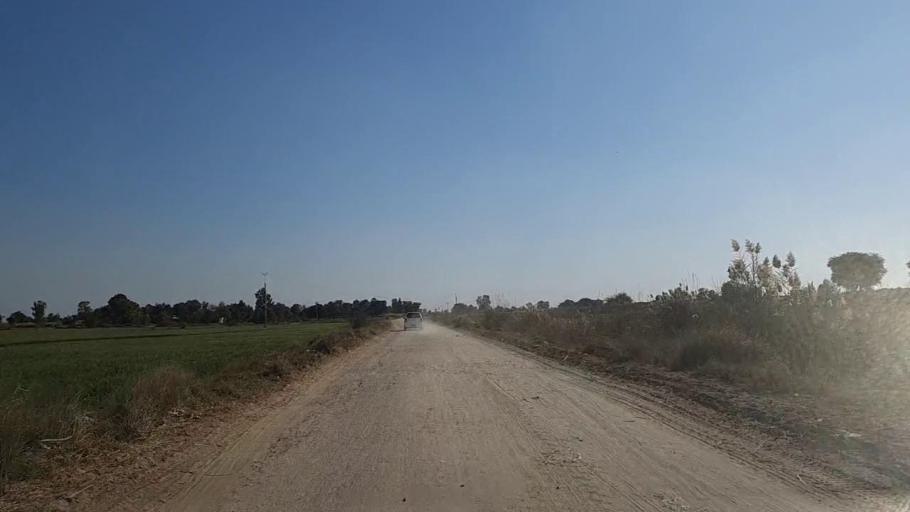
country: PK
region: Sindh
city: Nawabshah
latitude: 26.2340
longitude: 68.4260
